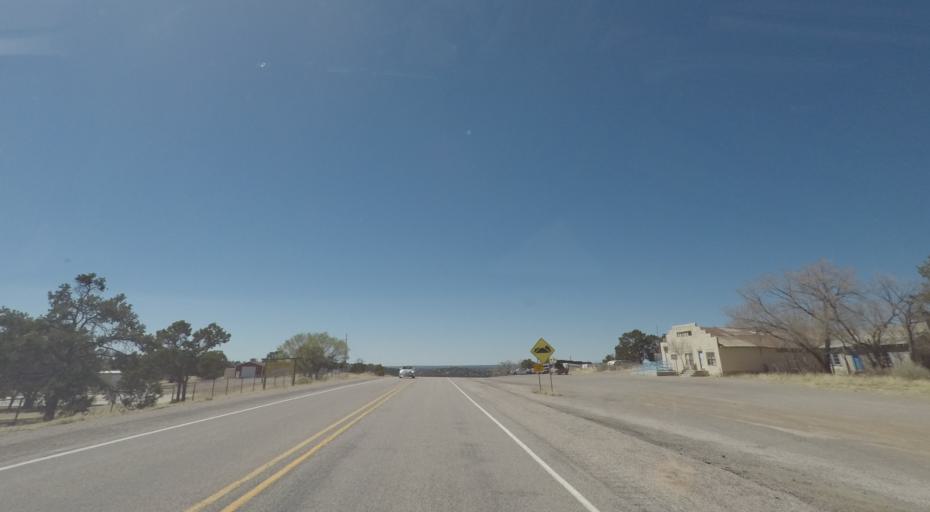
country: US
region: New Mexico
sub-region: Socorro County
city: Alamo
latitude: 34.2991
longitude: -108.1315
